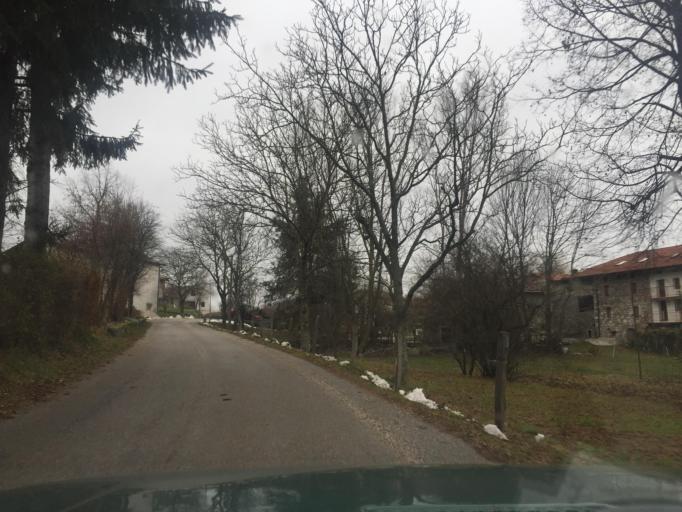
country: SI
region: Kanal
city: Kanal
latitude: 46.0764
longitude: 13.6644
